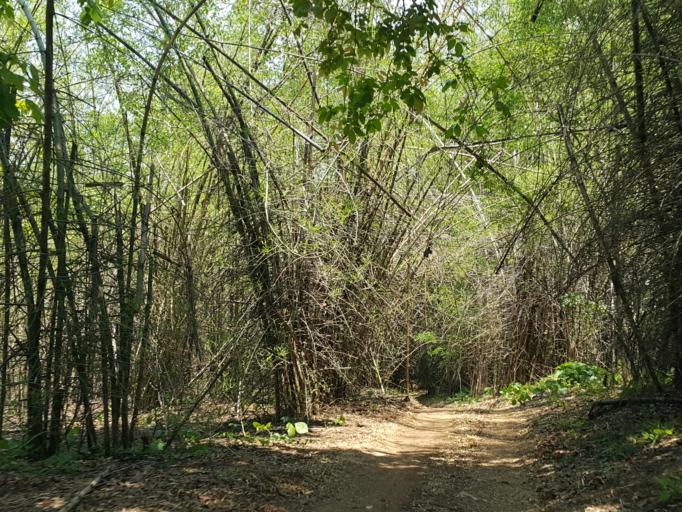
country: TH
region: Kanchanaburi
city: Sai Yok
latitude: 14.2111
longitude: 98.8805
